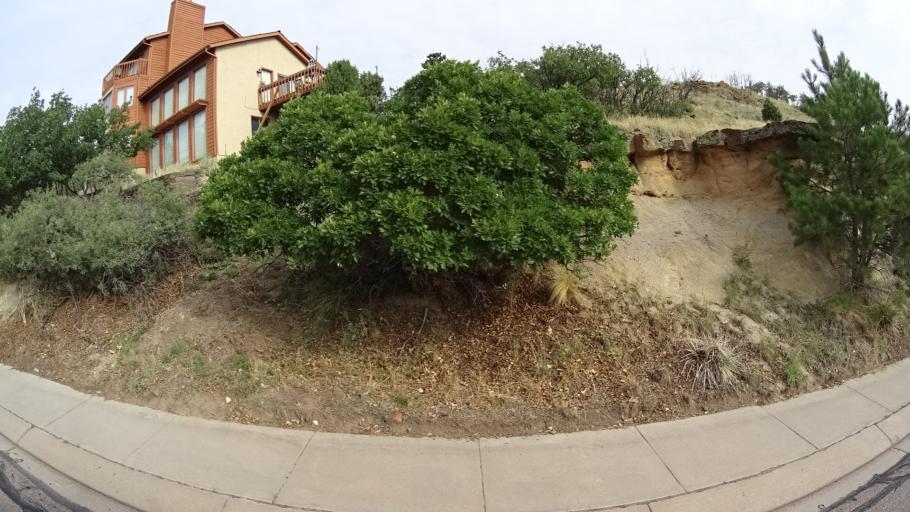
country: US
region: Colorado
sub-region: El Paso County
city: Air Force Academy
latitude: 38.9344
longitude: -104.8558
